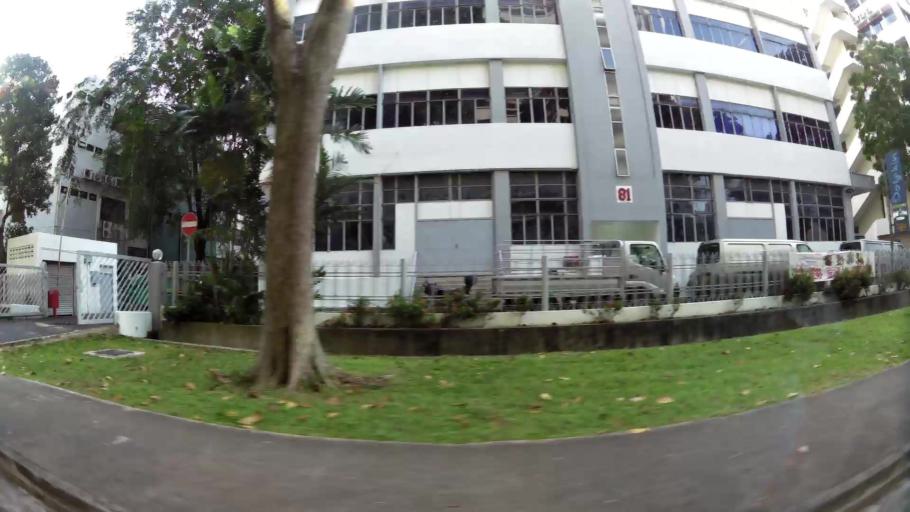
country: SG
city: Singapore
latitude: 1.3267
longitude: 103.8760
